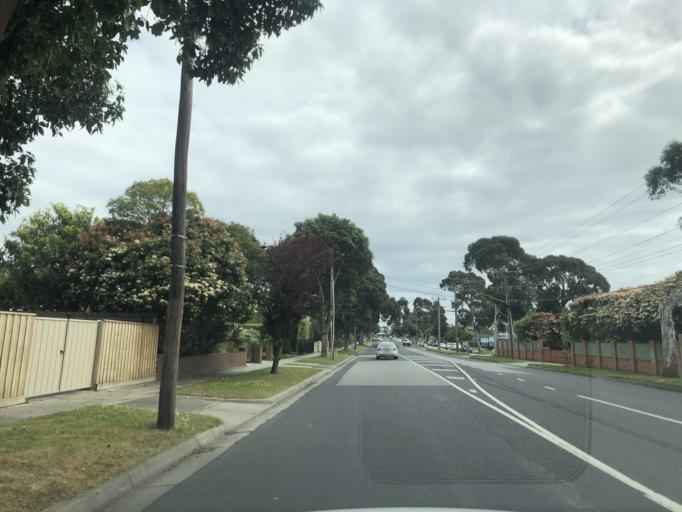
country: AU
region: Victoria
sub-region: Greater Dandenong
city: Noble Park North
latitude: -37.9386
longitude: 145.2042
